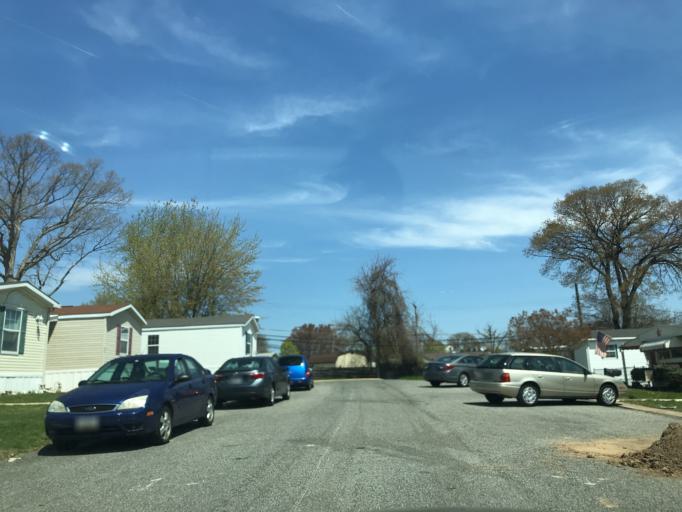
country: US
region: Maryland
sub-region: Baltimore County
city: Middle River
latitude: 39.3305
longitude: -76.4588
